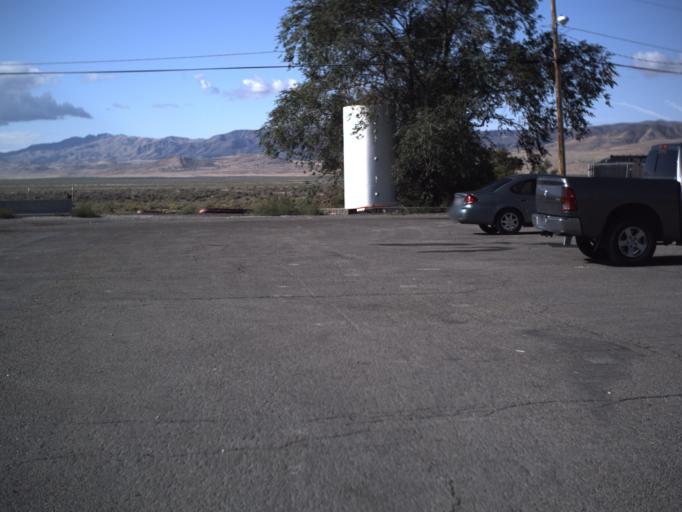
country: US
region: Utah
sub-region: Tooele County
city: Grantsville
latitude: 40.7619
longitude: -112.7826
